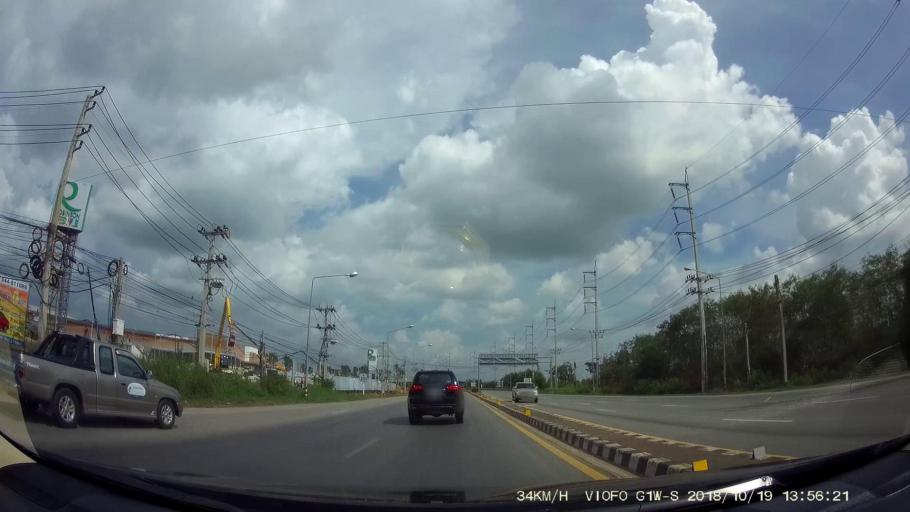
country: TH
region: Chaiyaphum
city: Chaiyaphum
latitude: 15.7862
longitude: 102.0291
